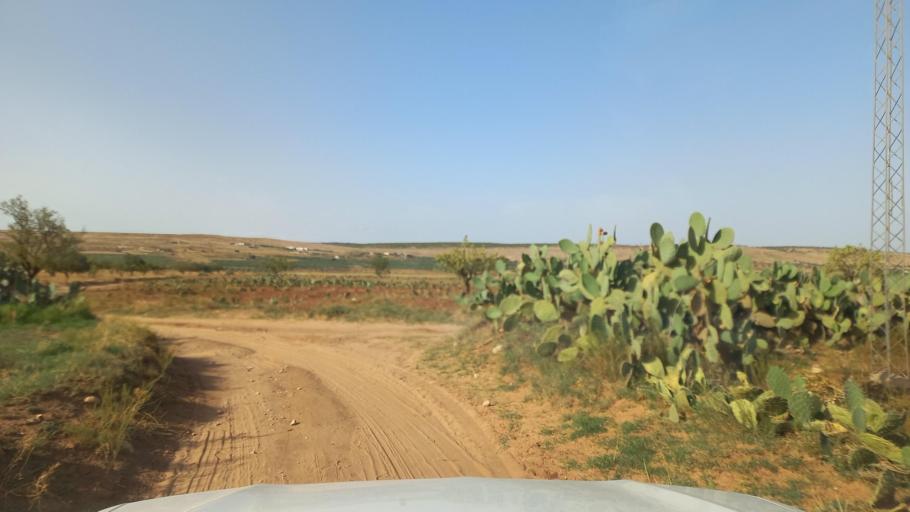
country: TN
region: Al Qasrayn
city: Kasserine
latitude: 35.3499
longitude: 8.8487
